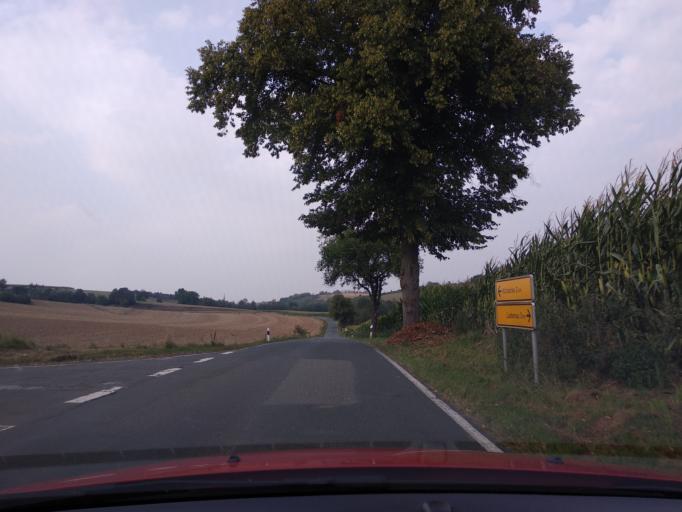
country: DE
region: Hesse
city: Liebenau
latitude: 51.5164
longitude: 9.2751
